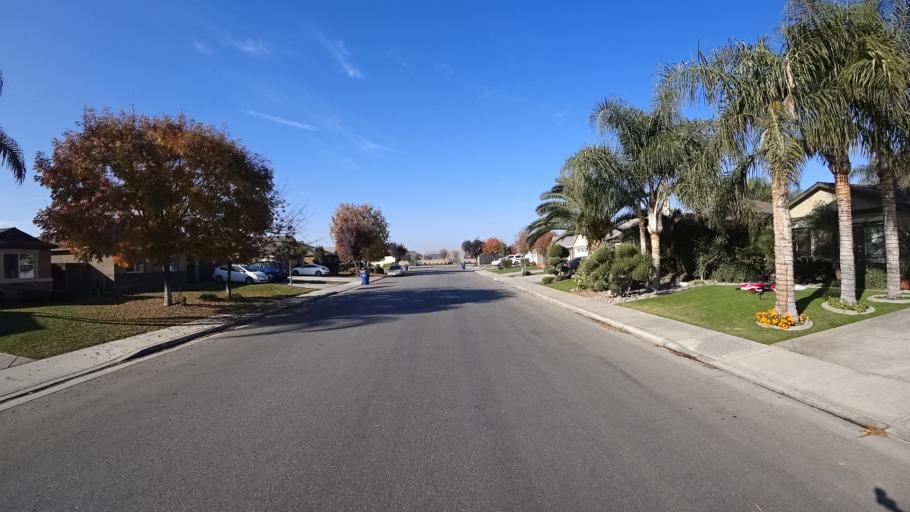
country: US
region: California
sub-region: Kern County
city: Greenfield
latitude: 35.2711
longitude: -119.0644
